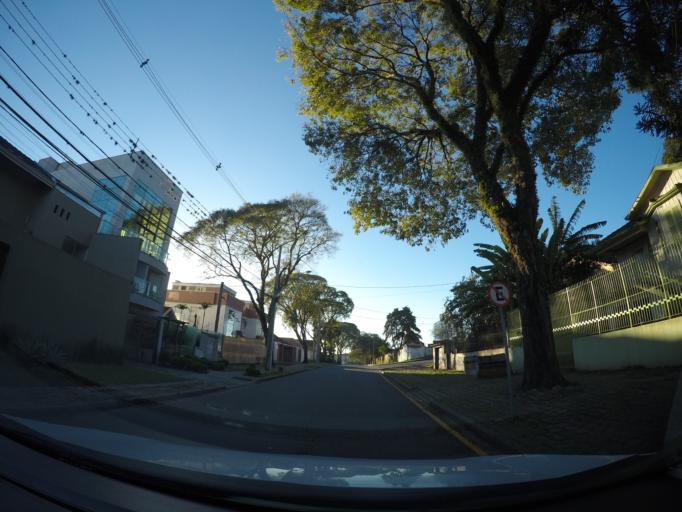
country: BR
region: Parana
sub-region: Curitiba
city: Curitiba
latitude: -25.4178
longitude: -49.2790
